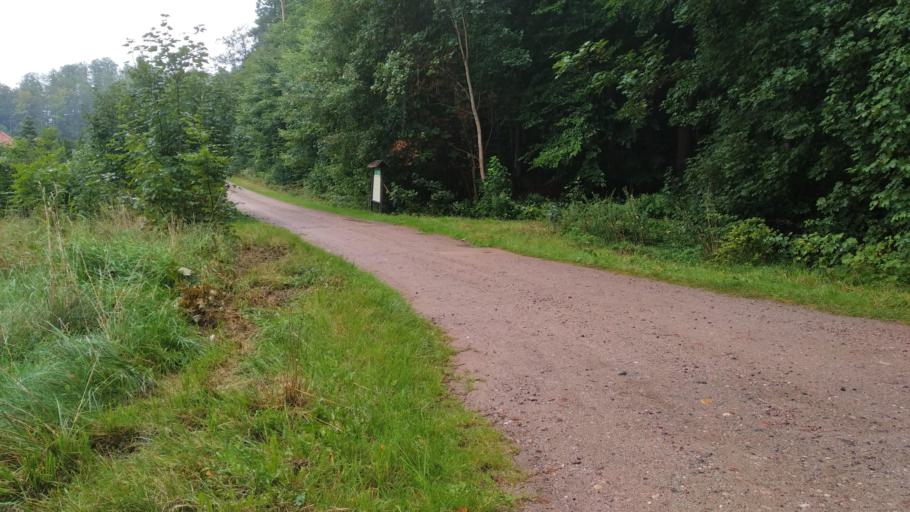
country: PL
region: Pomeranian Voivodeship
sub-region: Powiat wejherowski
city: Goscicino
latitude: 54.6348
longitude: 18.1321
